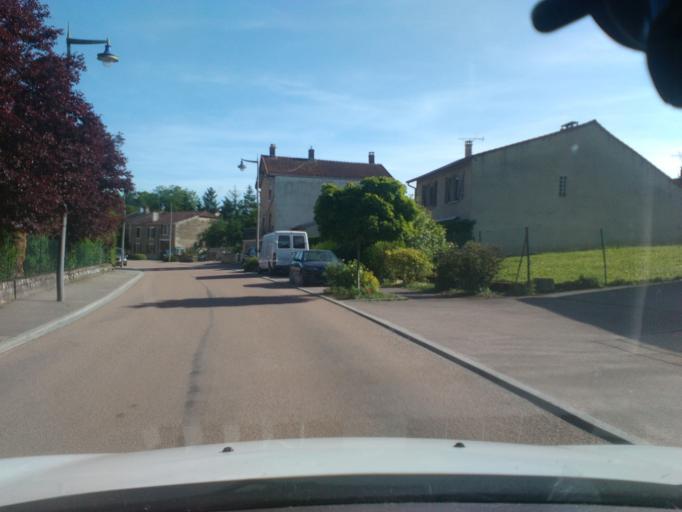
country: FR
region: Lorraine
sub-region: Departement des Vosges
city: Mirecourt
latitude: 48.2242
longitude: 6.2193
